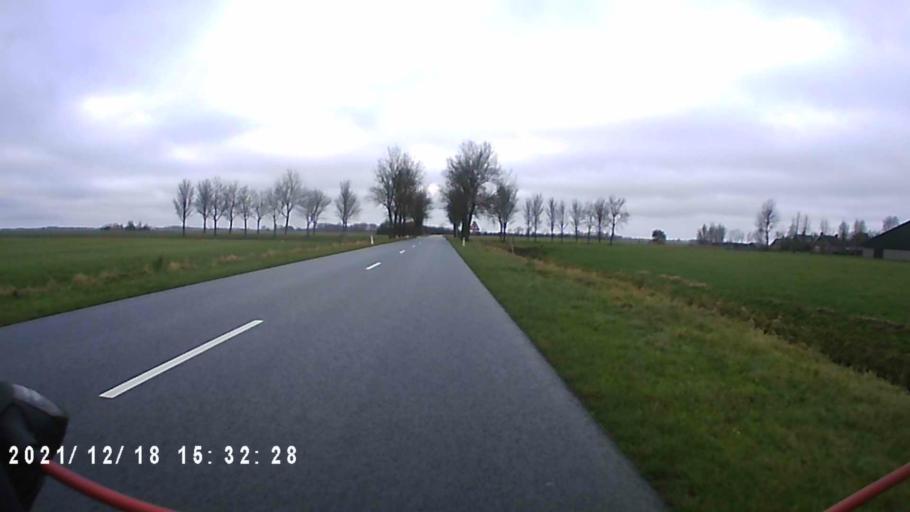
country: NL
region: Friesland
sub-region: Gemeente Dongeradeel
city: Anjum
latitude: 53.3419
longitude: 6.1346
